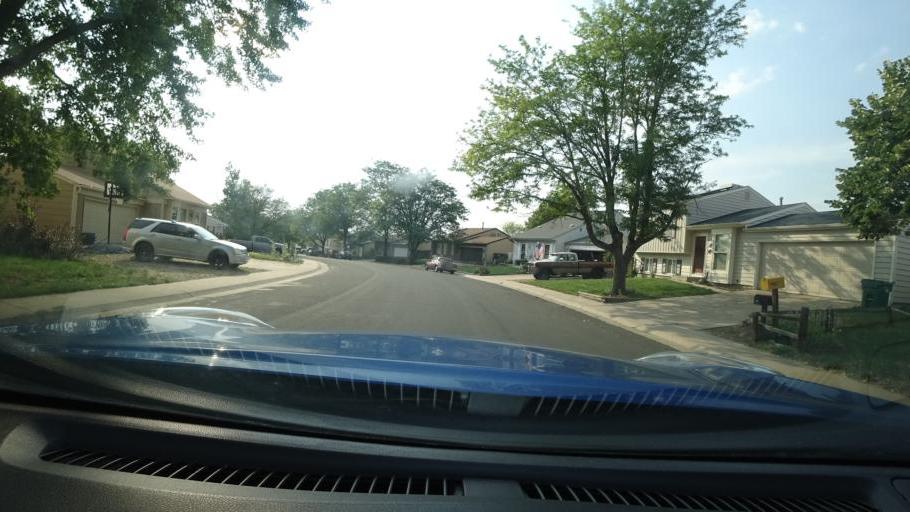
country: US
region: Colorado
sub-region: Adams County
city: Aurora
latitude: 39.7444
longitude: -104.7546
